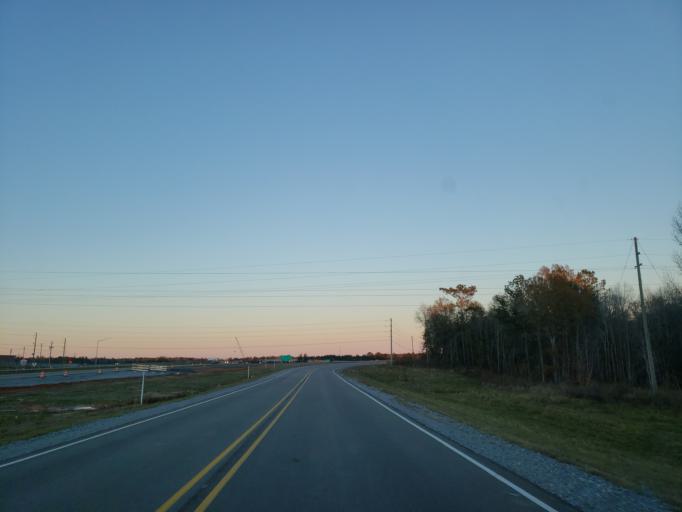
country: US
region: Mississippi
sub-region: Forrest County
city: Glendale
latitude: 31.3756
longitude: -89.3284
